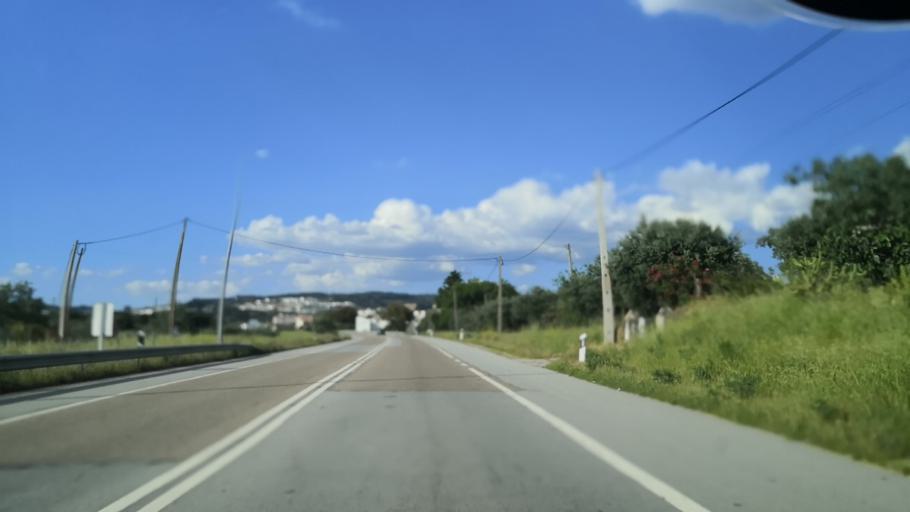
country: PT
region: Portalegre
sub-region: Portalegre
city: Portalegre
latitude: 39.2730
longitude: -7.4369
